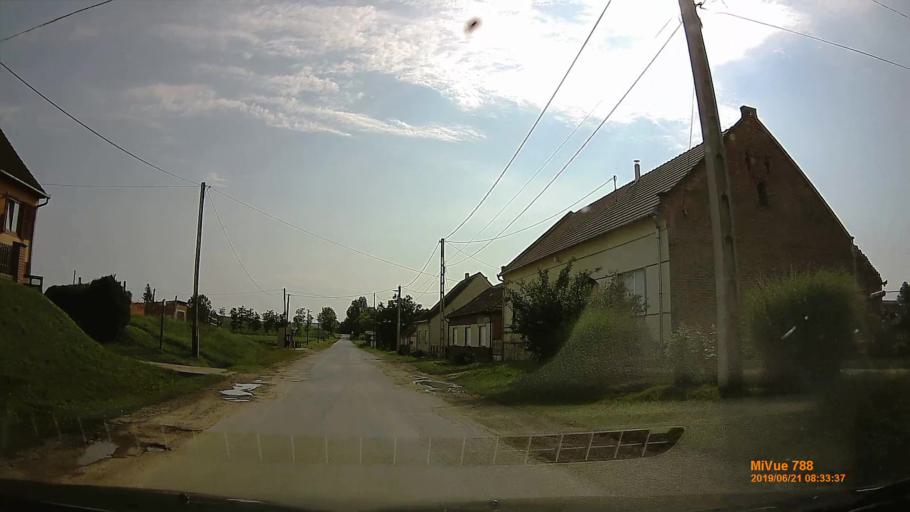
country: HU
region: Baranya
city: Buekkoesd
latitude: 46.1627
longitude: 17.8818
